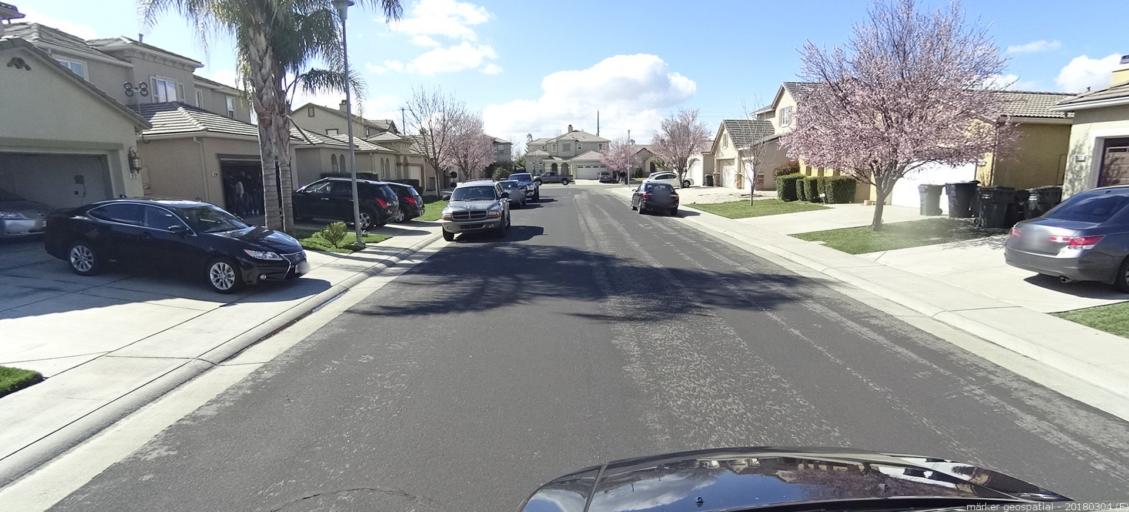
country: US
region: California
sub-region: Sacramento County
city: Vineyard
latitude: 38.4653
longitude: -121.3332
